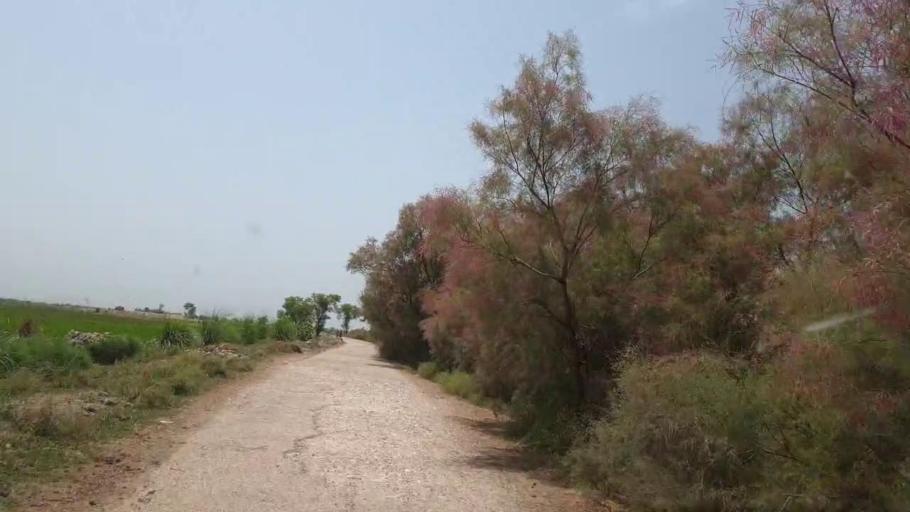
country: PK
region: Sindh
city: Shikarpur
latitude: 27.9081
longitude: 68.6337
